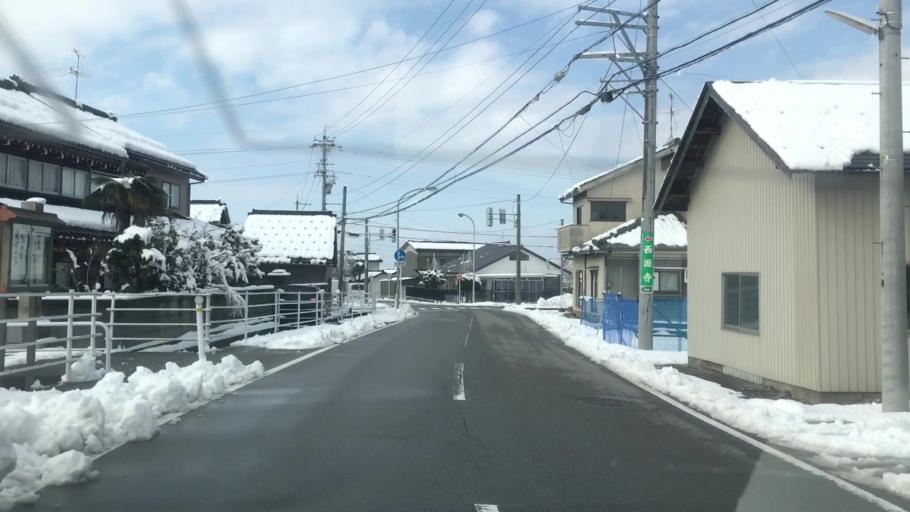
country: JP
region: Toyama
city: Toyama-shi
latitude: 36.6161
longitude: 137.2760
